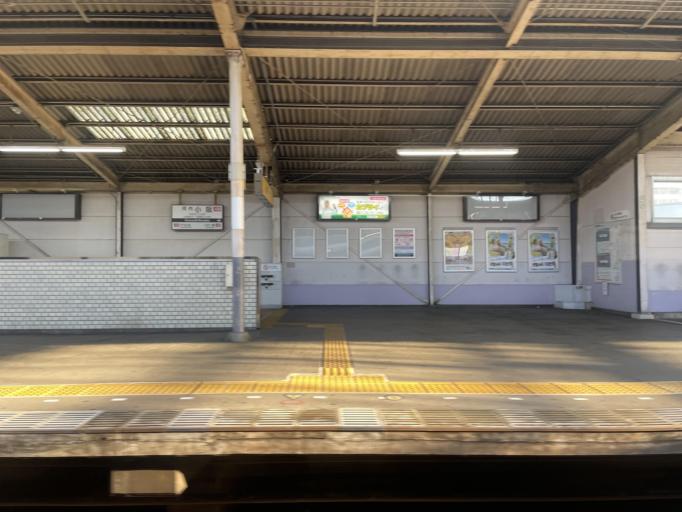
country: JP
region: Osaka
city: Yao
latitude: 34.6641
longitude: 135.5816
